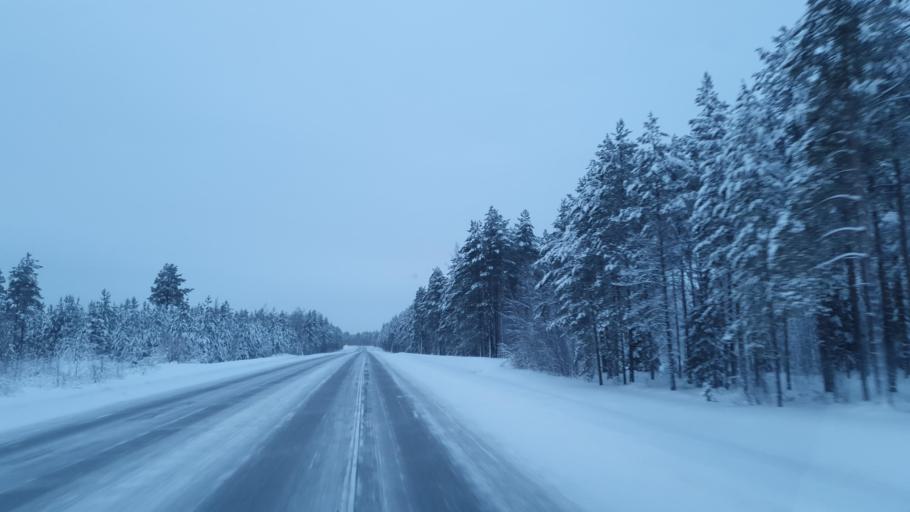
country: FI
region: Kainuu
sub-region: Kajaani
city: Vaala
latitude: 64.5879
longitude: 26.8136
